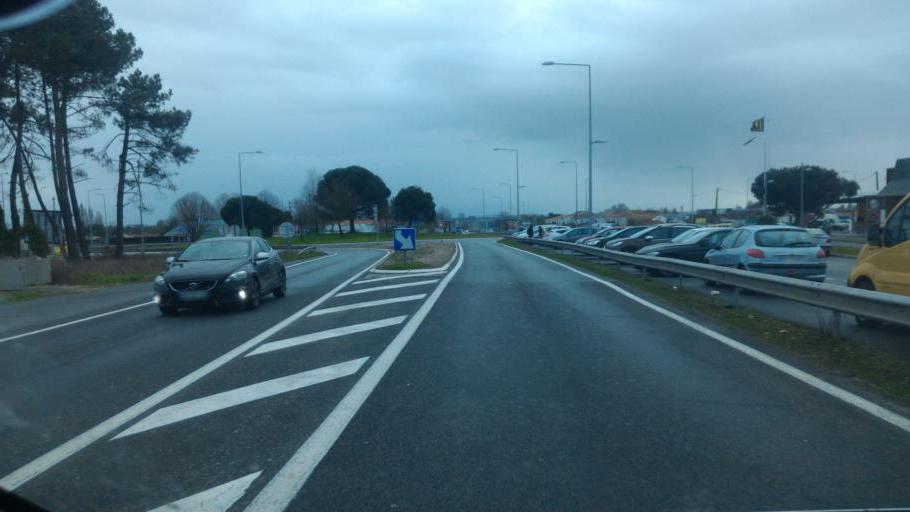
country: FR
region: Aquitaine
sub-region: Departement de la Gironde
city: Saint-Gervais
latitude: 45.0064
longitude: -0.4372
